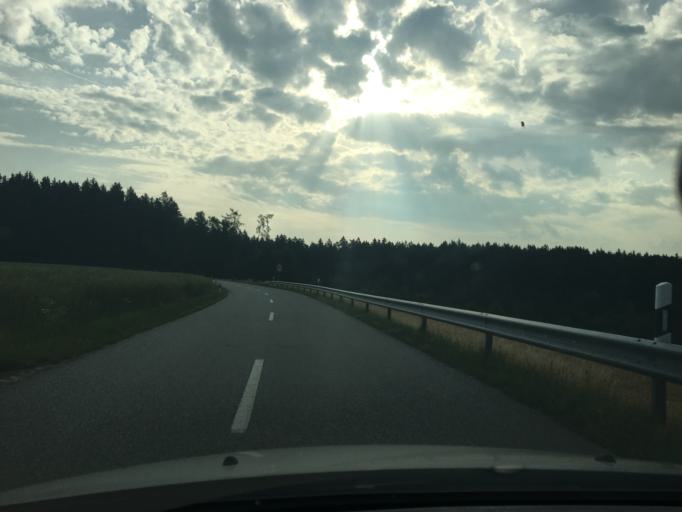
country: DE
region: Bavaria
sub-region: Lower Bavaria
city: Bodenkirchen
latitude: 48.3805
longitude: 12.3952
